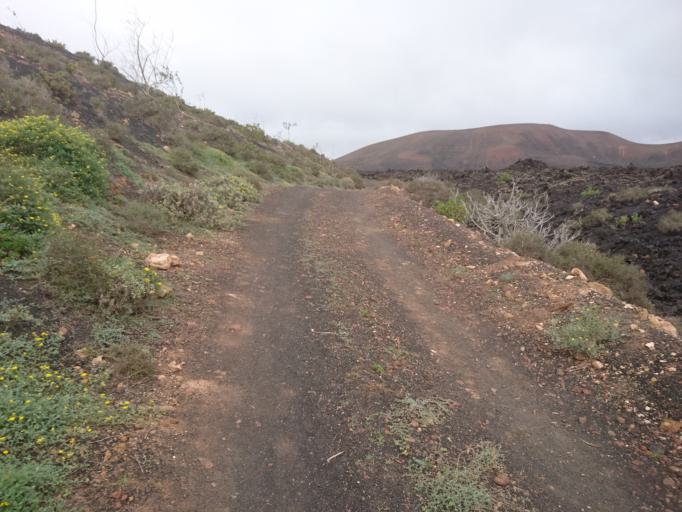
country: ES
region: Canary Islands
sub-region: Provincia de Las Palmas
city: Tinajo
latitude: 29.0163
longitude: -13.6935
